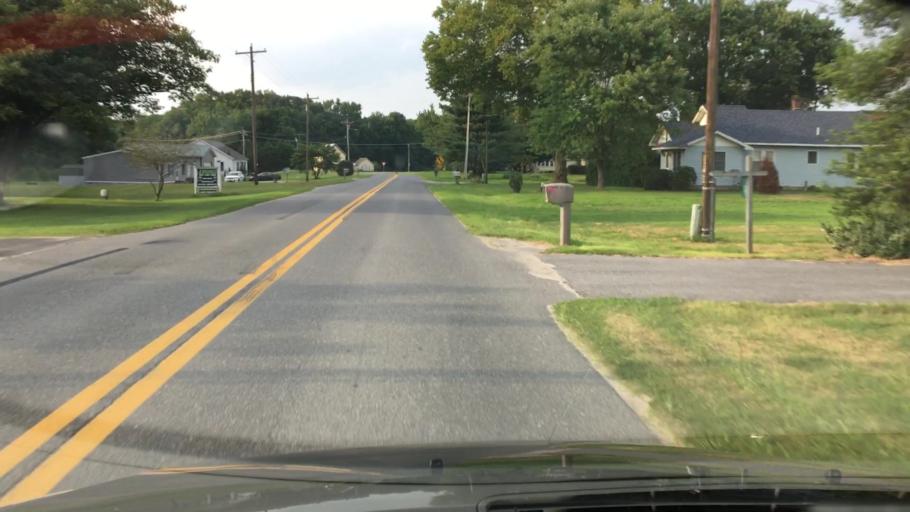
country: US
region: Maryland
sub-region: Worcester County
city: Ocean Pines
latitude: 38.4729
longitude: -75.1395
